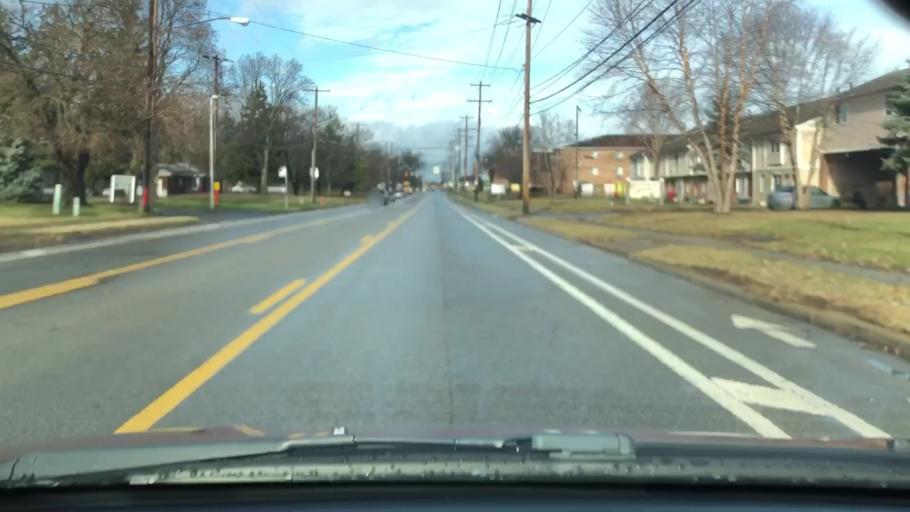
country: US
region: Ohio
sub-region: Franklin County
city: Minerva Park
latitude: 40.0483
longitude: -82.9768
